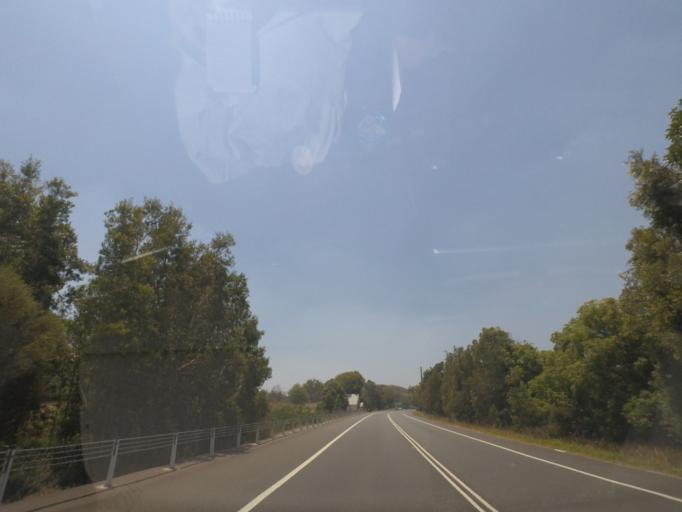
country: AU
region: New South Wales
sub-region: Port Stephens Shire
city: Medowie
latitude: -32.8071
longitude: 151.8600
